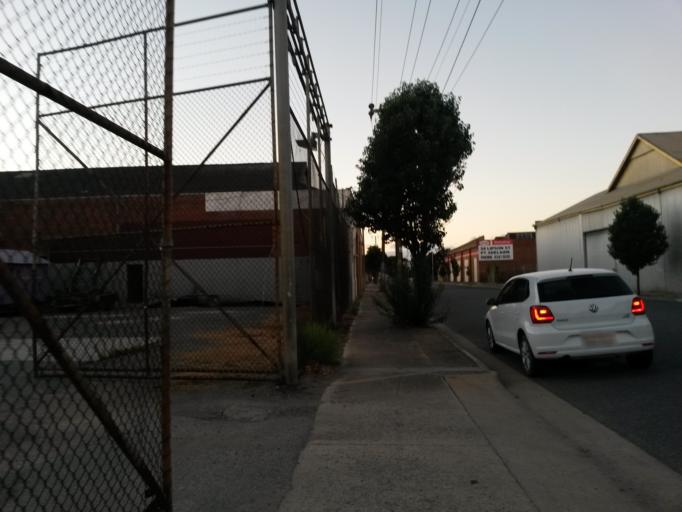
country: AU
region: South Australia
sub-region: Port Adelaide Enfield
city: Alberton
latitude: -34.8488
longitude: 138.5097
